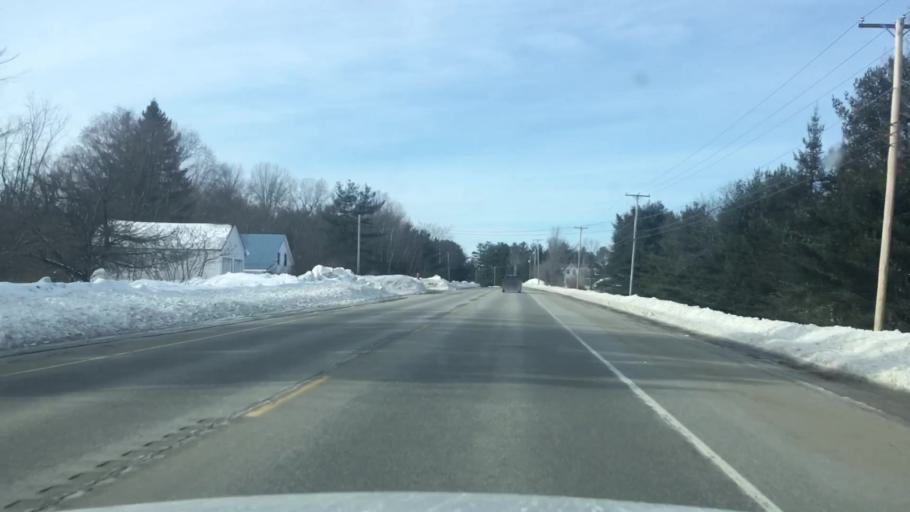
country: US
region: Maine
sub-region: Penobscot County
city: Kenduskeag
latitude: 44.9564
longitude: -68.9521
